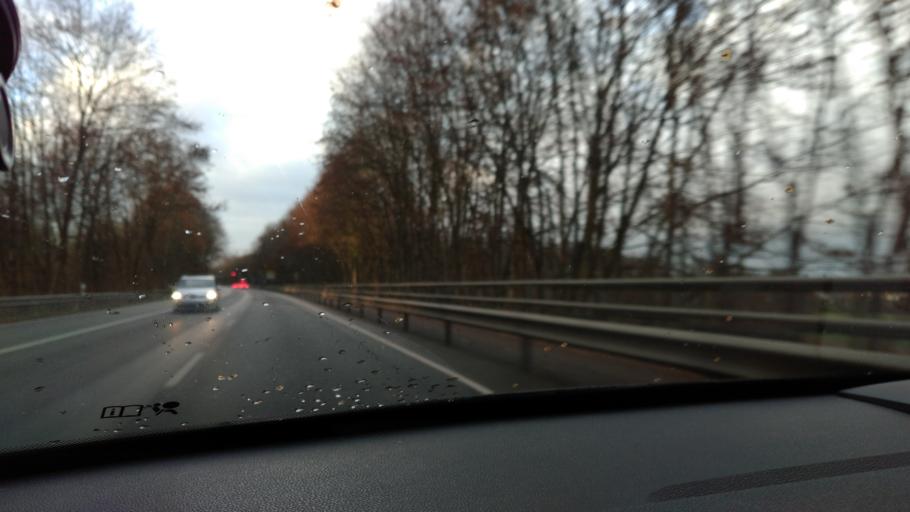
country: DE
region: North Rhine-Westphalia
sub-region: Regierungsbezirk Koln
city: Bonn
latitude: 50.7688
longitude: 7.1005
